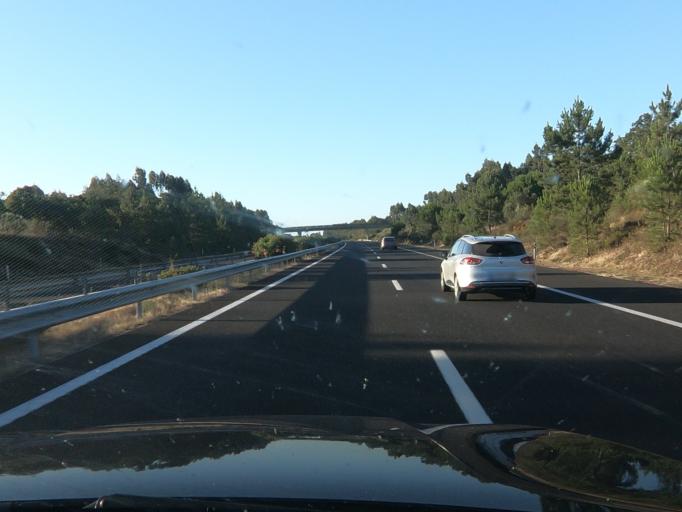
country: PT
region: Santarem
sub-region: Benavente
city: Poceirao
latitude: 38.7360
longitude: -8.6784
